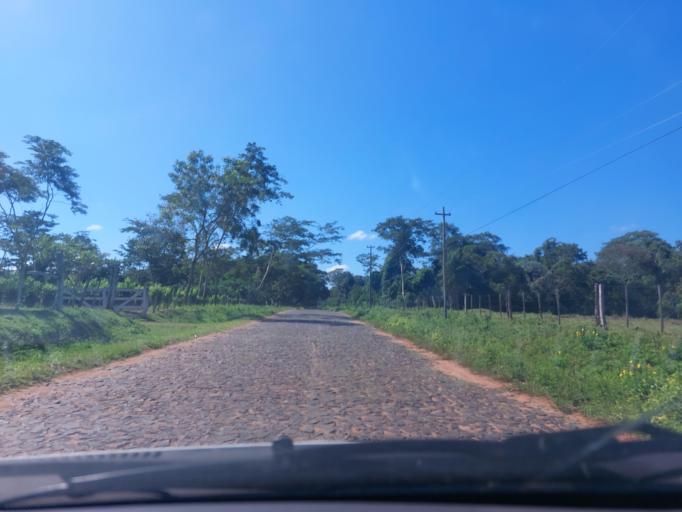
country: PY
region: San Pedro
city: Itacurubi del Rosario
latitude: -24.5743
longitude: -56.5984
